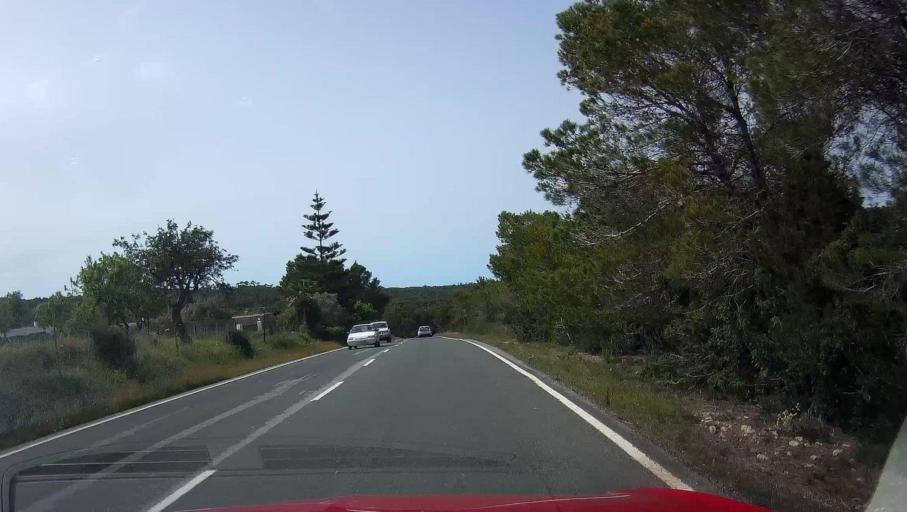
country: ES
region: Balearic Islands
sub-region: Illes Balears
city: Sant Joan de Labritja
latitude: 39.0927
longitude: 1.5005
